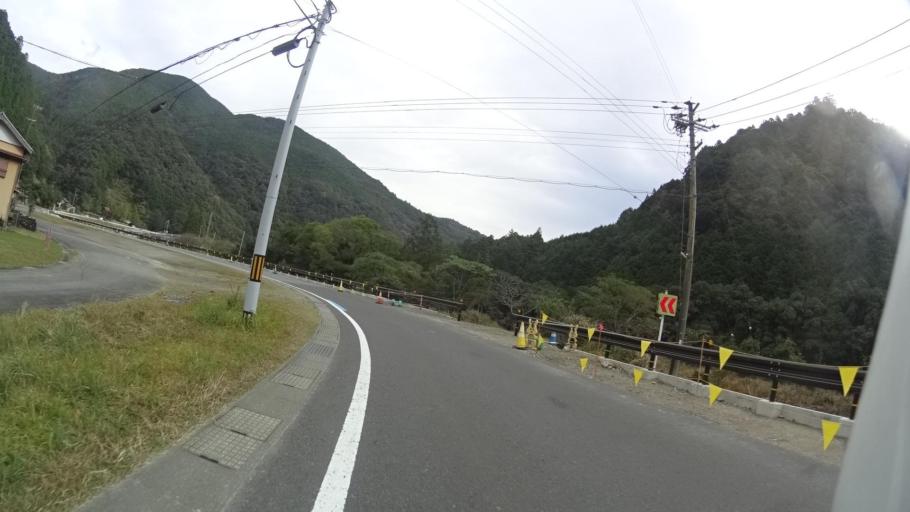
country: JP
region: Wakayama
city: Shingu
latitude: 33.5498
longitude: 135.6992
